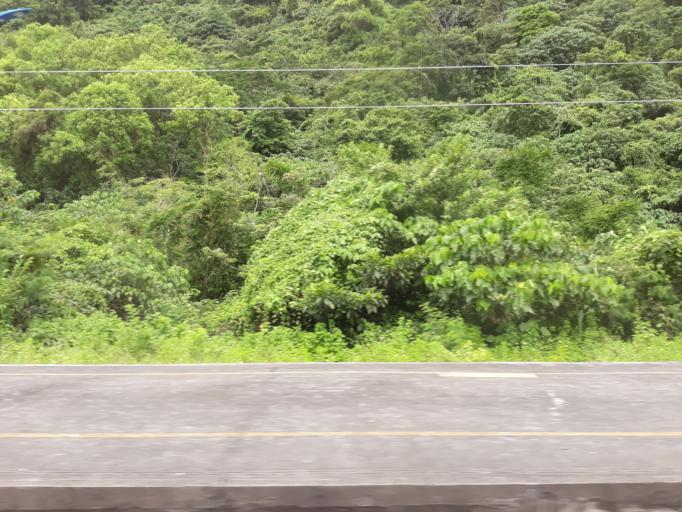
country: TW
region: Taiwan
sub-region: Yilan
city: Yilan
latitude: 24.4496
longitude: 121.7756
